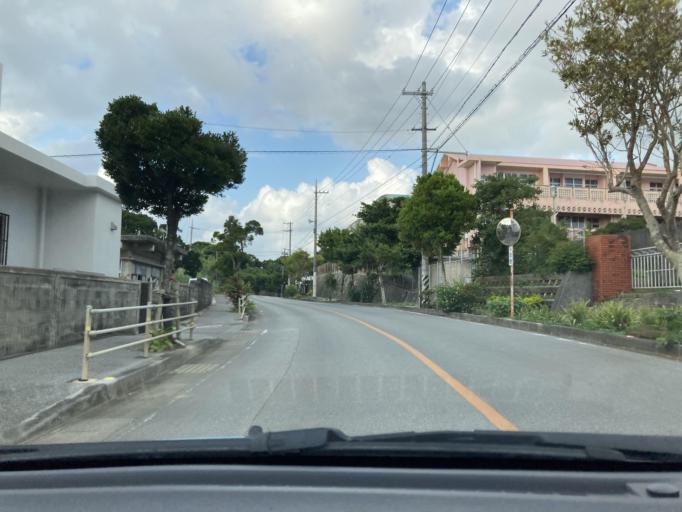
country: JP
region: Okinawa
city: Itoman
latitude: 26.0938
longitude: 127.6642
